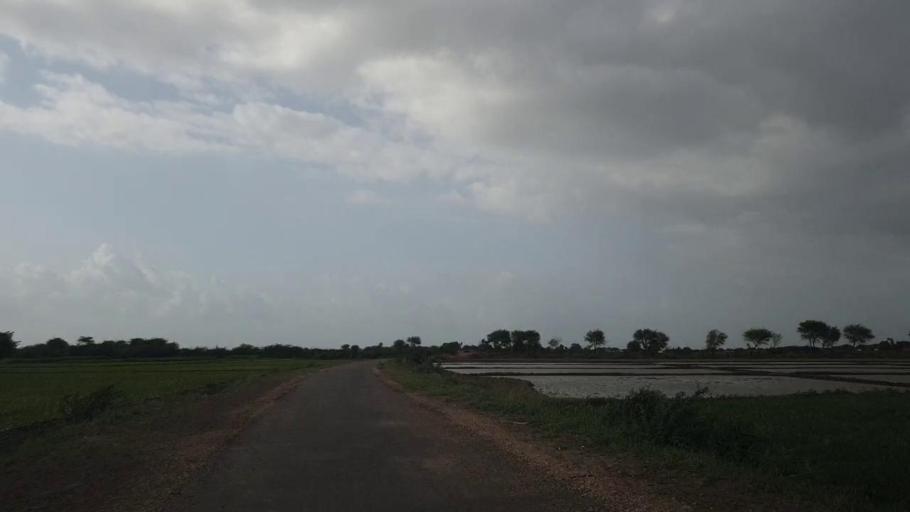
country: PK
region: Sindh
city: Kadhan
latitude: 24.6021
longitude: 69.0554
